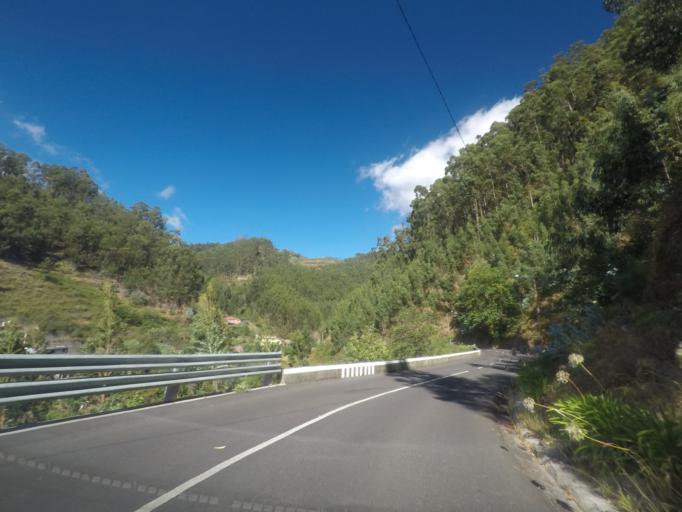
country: PT
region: Madeira
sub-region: Ribeira Brava
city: Campanario
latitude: 32.6875
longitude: -17.0304
